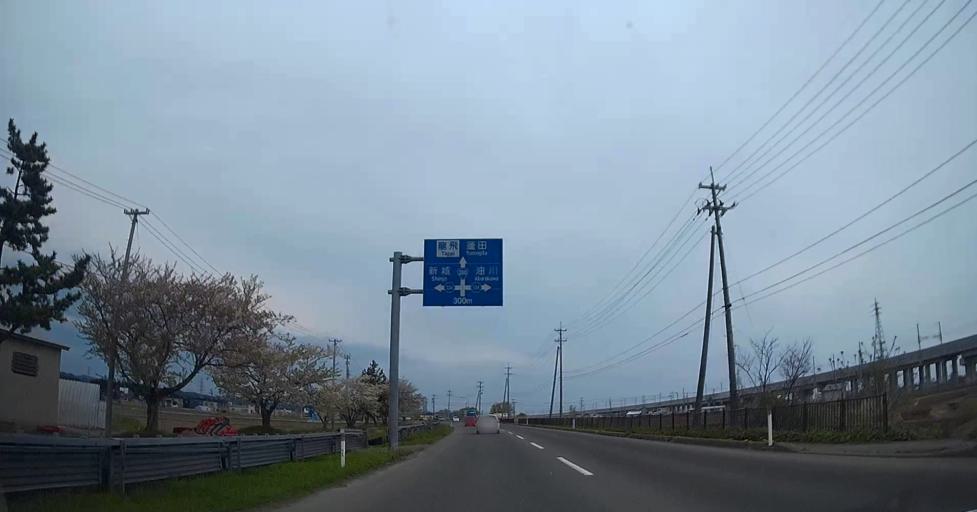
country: JP
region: Aomori
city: Aomori Shi
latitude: 40.8416
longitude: 140.6895
